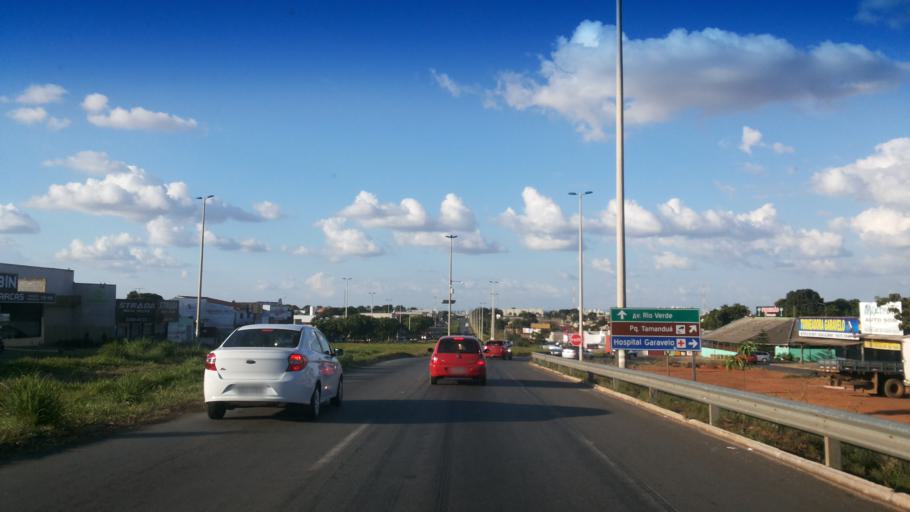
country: BR
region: Goias
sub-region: Aparecida De Goiania
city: Aparecida de Goiania
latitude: -16.7611
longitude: -49.3452
